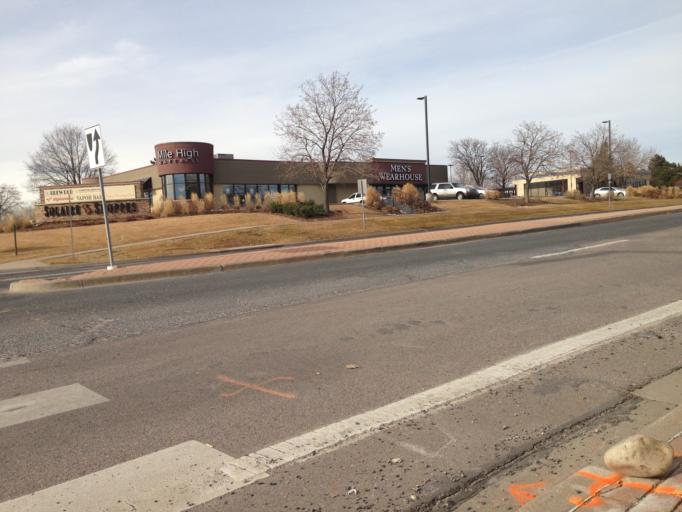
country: US
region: Colorado
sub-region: Adams County
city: Westminster
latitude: 39.8567
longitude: -105.0633
